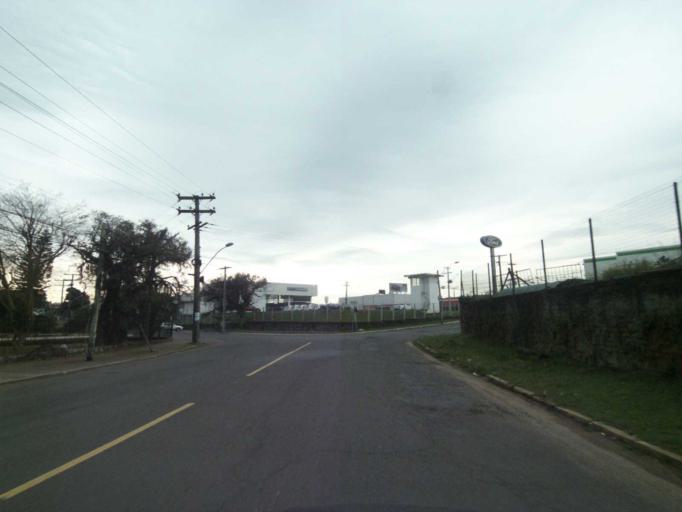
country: BR
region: Rio Grande do Sul
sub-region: Sao Leopoldo
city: Sao Leopoldo
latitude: -29.7797
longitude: -51.1587
